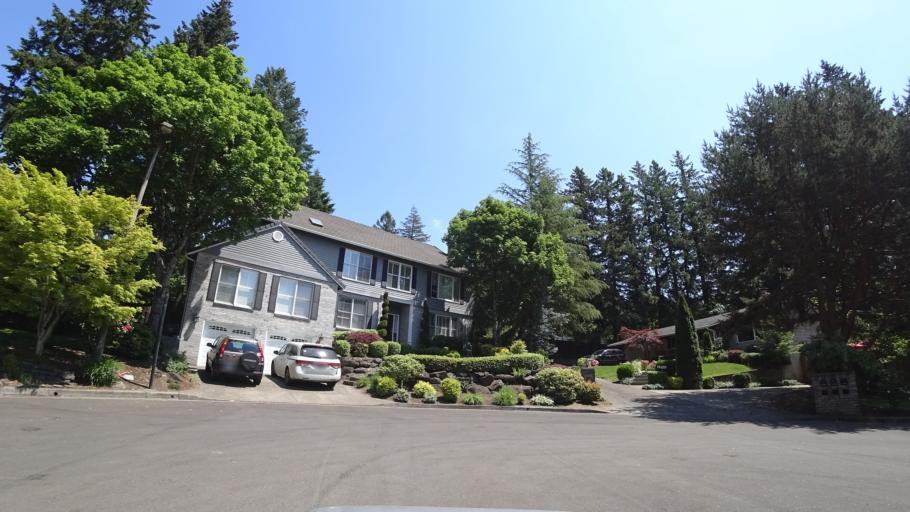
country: US
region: Oregon
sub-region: Washington County
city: Metzger
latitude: 45.4292
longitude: -122.7265
